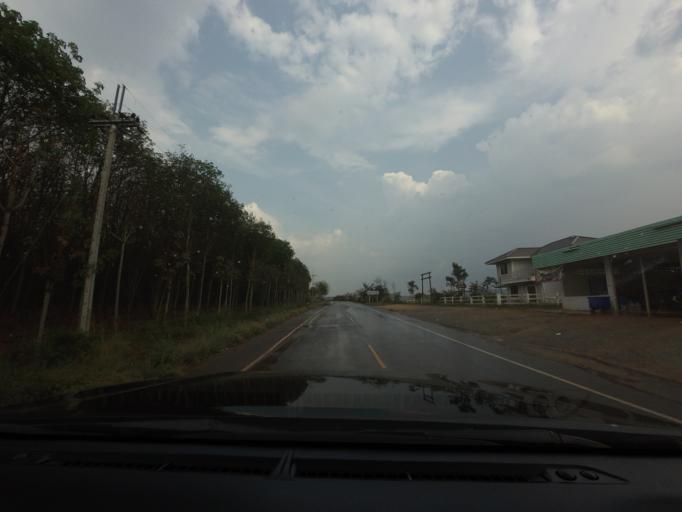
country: TH
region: Nakhon Ratchasima
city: Wang Nam Khiao
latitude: 14.4098
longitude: 101.7391
